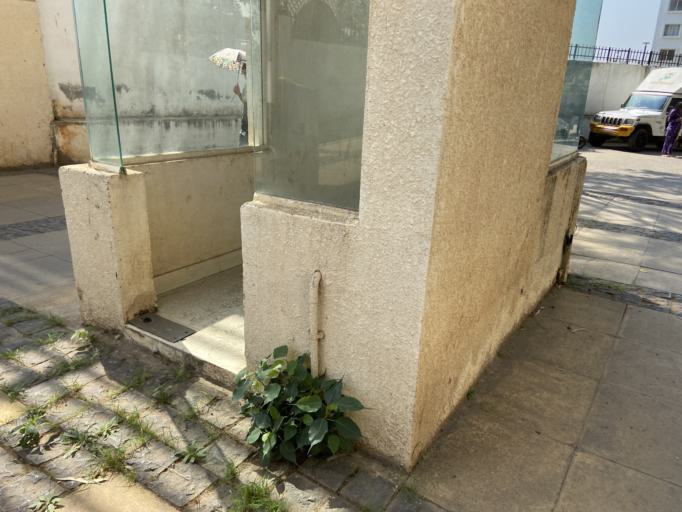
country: IN
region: Karnataka
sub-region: Bangalore Urban
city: Bangalore
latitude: 12.9481
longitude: 77.6778
